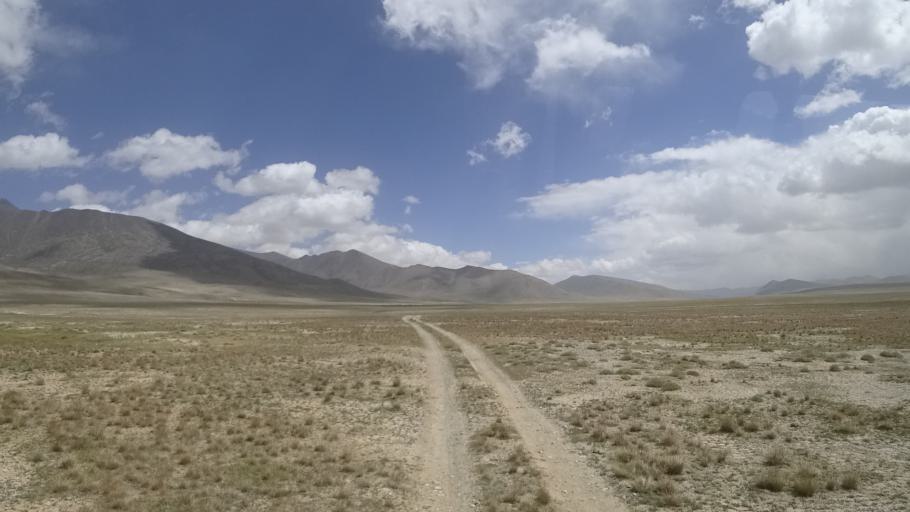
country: TJ
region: Gorno-Badakhshan
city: Murghob
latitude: 37.4806
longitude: 73.9805
